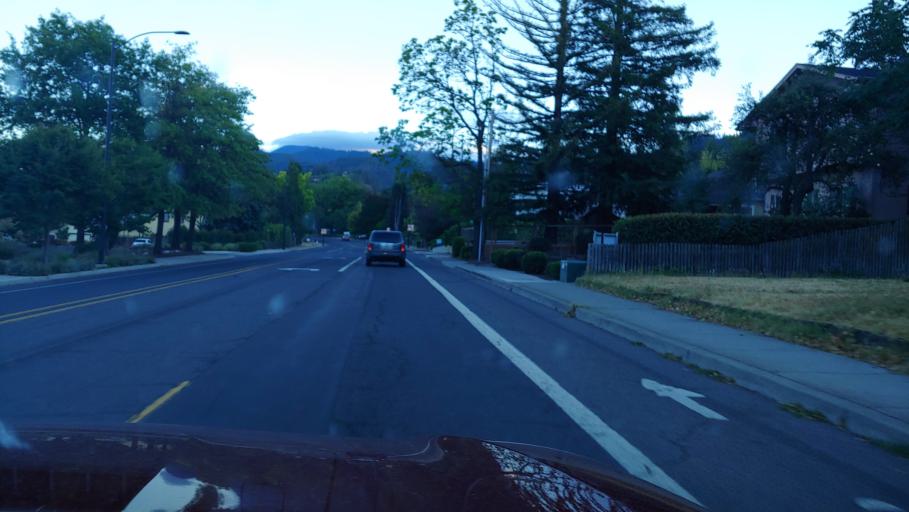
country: US
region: Oregon
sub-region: Jackson County
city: Ashland
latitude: 42.2045
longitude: -122.7200
